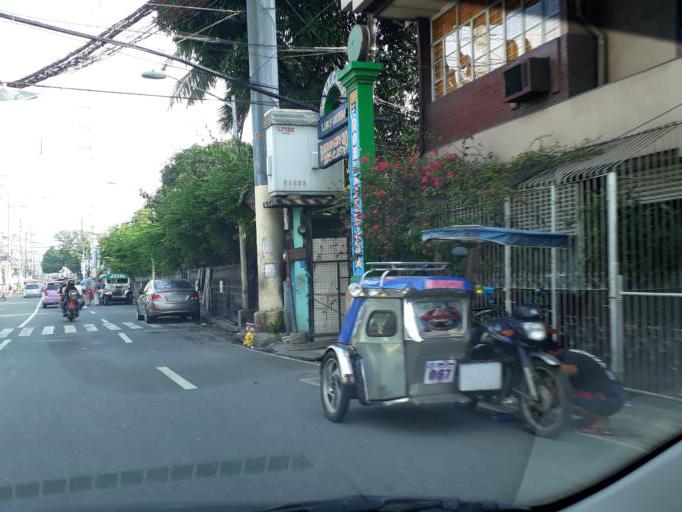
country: PH
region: Metro Manila
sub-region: Caloocan City
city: Niugan
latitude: 14.6477
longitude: 120.9735
